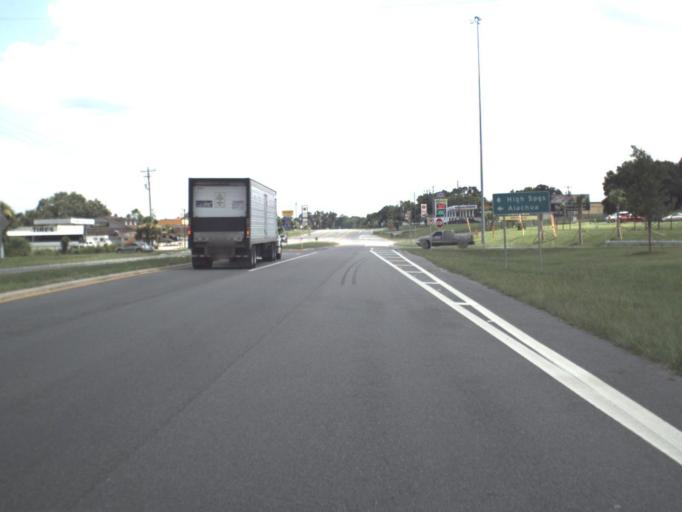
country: US
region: Florida
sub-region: Alachua County
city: High Springs
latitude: 29.9996
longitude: -82.5975
